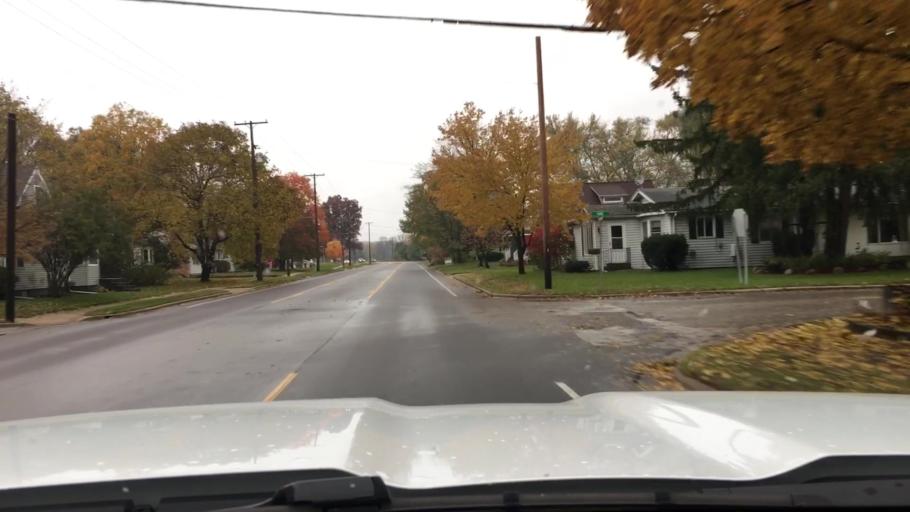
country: US
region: Michigan
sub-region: Kent County
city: Lowell
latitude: 42.9418
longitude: -85.3448
